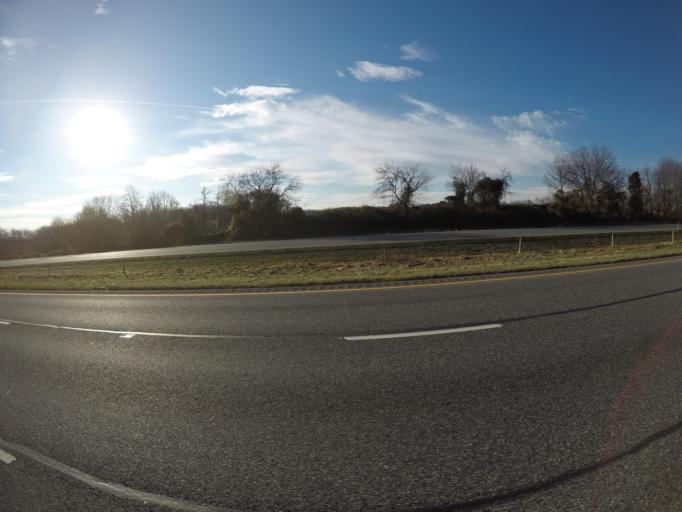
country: US
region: Maryland
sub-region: Carroll County
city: Sykesville
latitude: 39.3219
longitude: -76.9948
